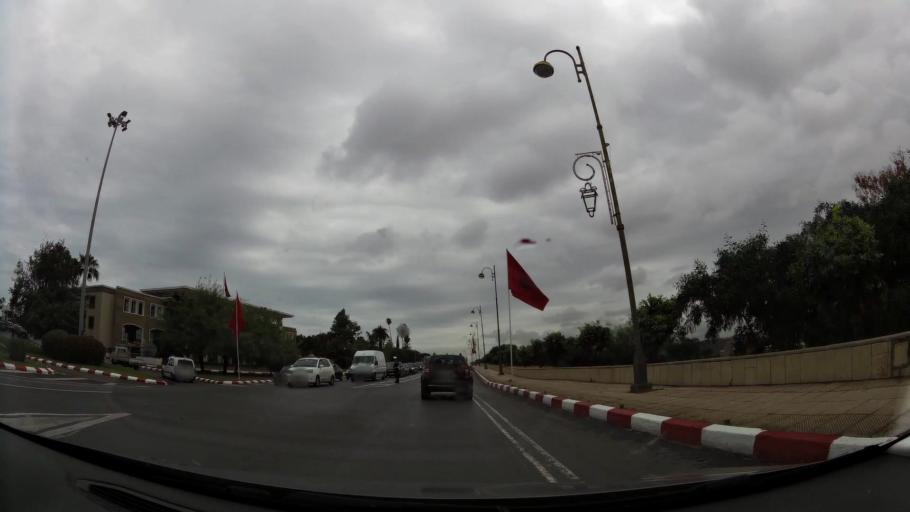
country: MA
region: Rabat-Sale-Zemmour-Zaer
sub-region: Rabat
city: Rabat
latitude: 34.0103
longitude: -6.8216
